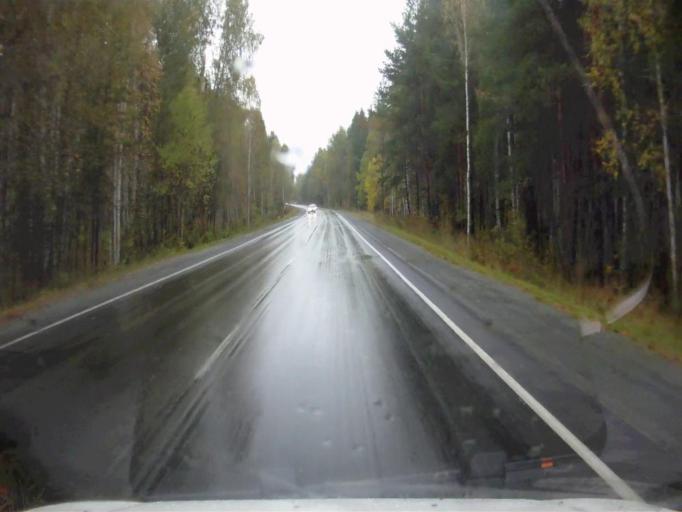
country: RU
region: Chelyabinsk
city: Tayginka
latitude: 55.5924
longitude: 60.6256
